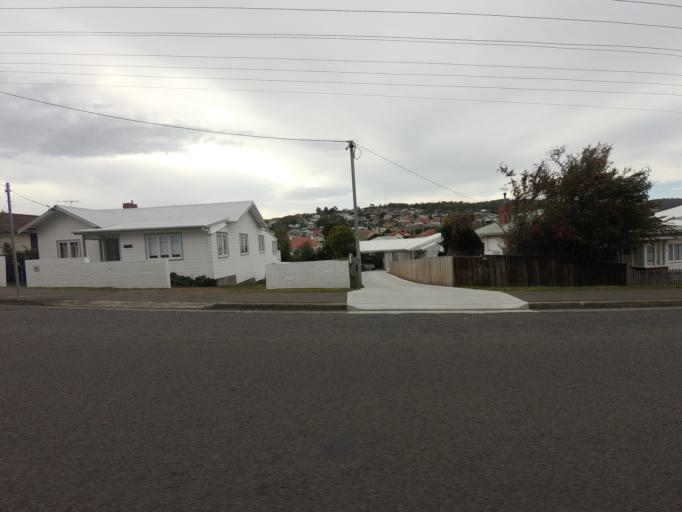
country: AU
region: Tasmania
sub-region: Clarence
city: Bellerive
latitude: -42.8767
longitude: 147.3746
